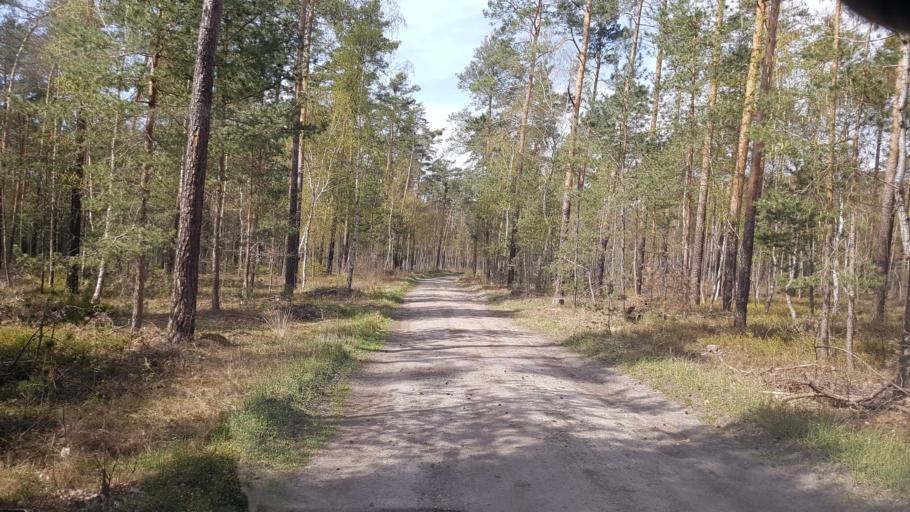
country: DE
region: Brandenburg
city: Plessa
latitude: 51.5442
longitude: 13.6593
